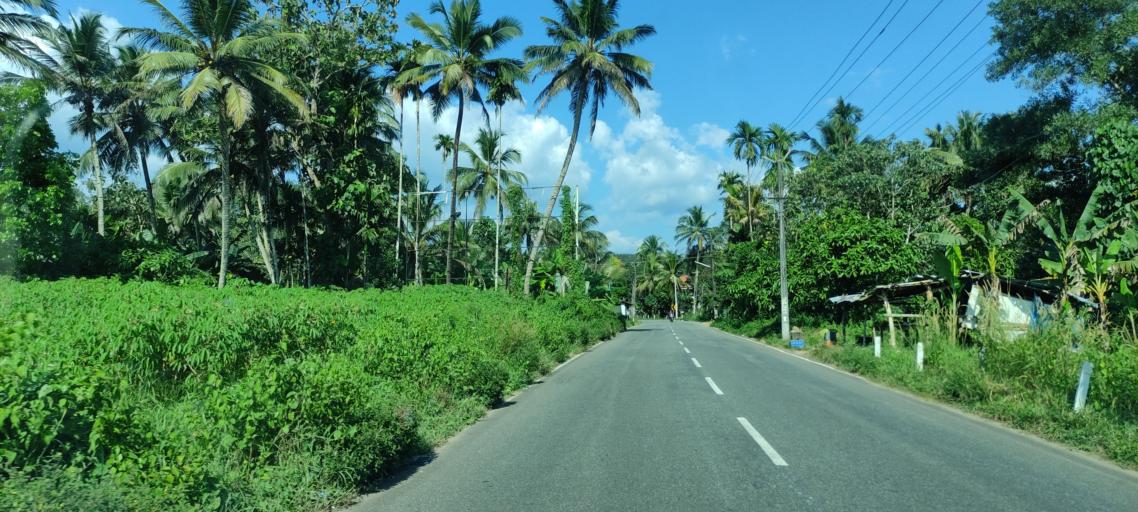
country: IN
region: Kerala
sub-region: Pattanamtitta
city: Adur
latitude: 9.2148
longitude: 76.7472
